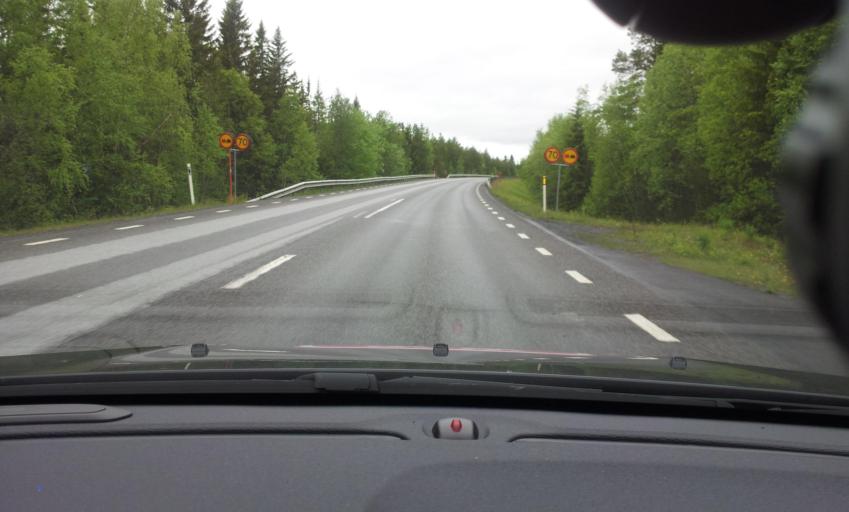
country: SE
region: Jaemtland
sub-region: Krokoms Kommun
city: Valla
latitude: 63.3059
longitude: 13.8422
